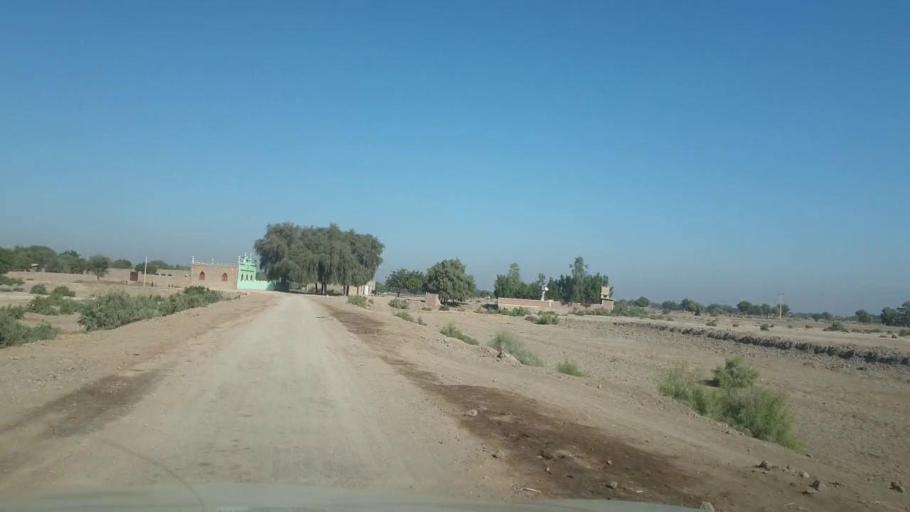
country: PK
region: Sindh
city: Bhan
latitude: 26.5473
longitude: 67.6561
